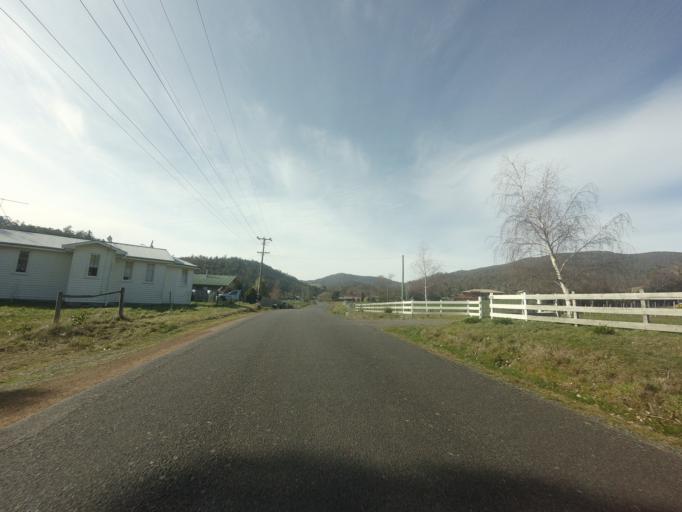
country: AU
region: Tasmania
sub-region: Huon Valley
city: Cygnet
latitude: -43.1808
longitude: 147.1270
